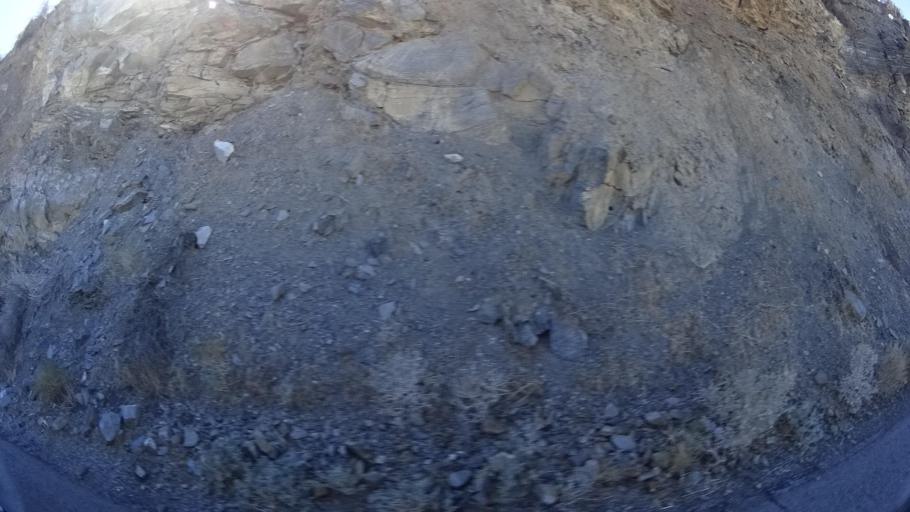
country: US
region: California
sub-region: Kern County
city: Ridgecrest
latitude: 35.3780
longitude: -117.6687
